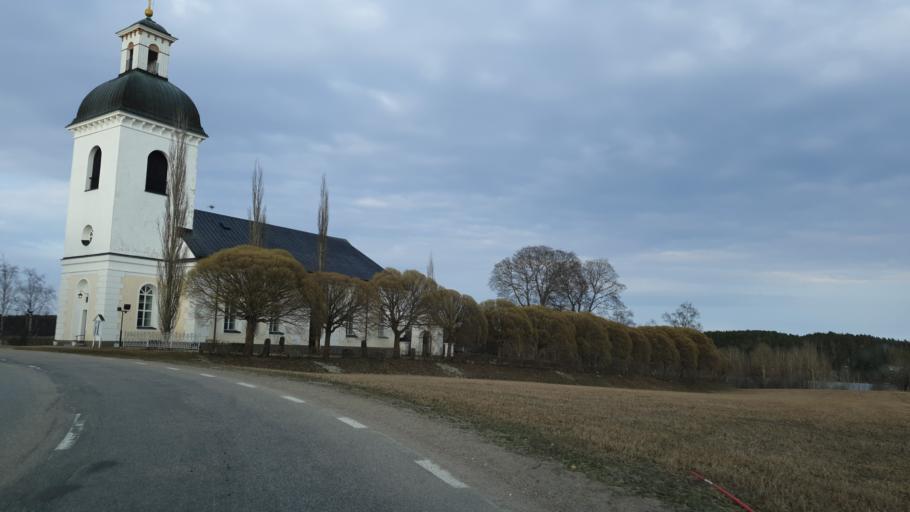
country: SE
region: Gaevleborg
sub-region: Nordanstigs Kommun
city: Bergsjoe
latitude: 61.9735
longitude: 17.2584
